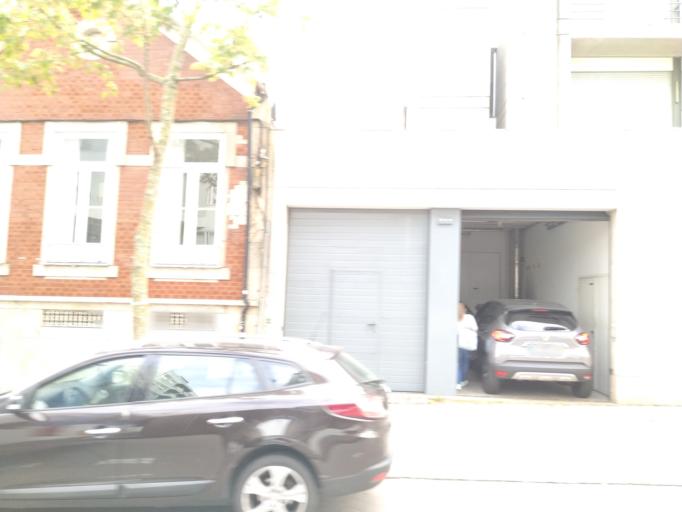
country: PT
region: Porto
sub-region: Porto
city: Porto
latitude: 41.1525
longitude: -8.6366
